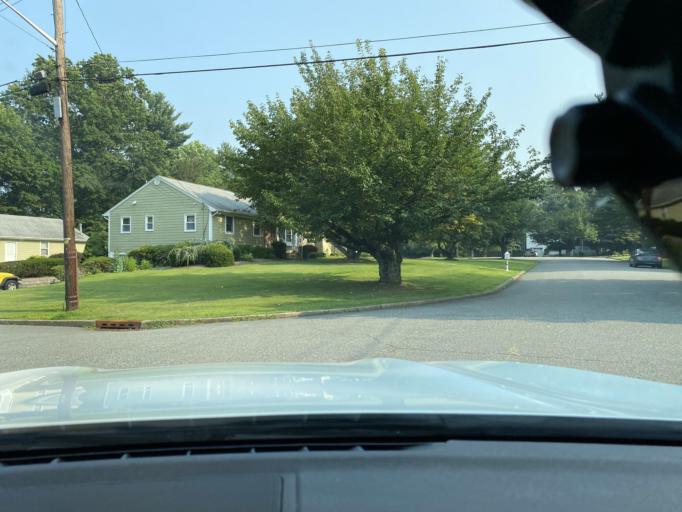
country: US
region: New York
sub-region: Rockland County
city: Airmont
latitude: 41.0969
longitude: -74.1296
